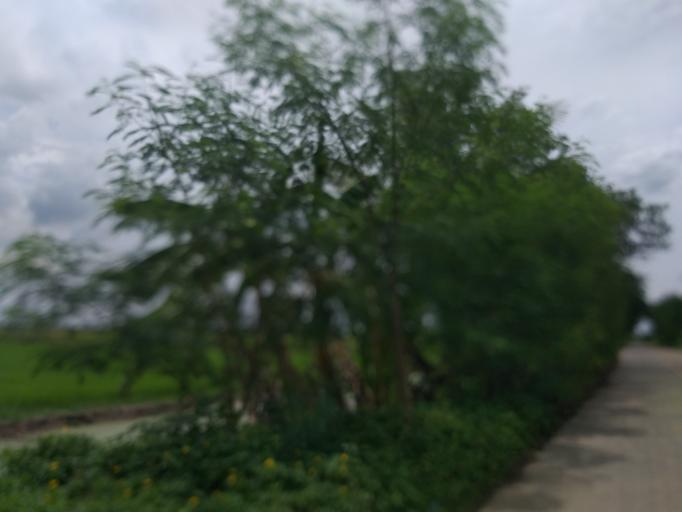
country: TH
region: Pathum Thani
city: Ban Lam Luk Ka
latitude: 14.0099
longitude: 100.8649
